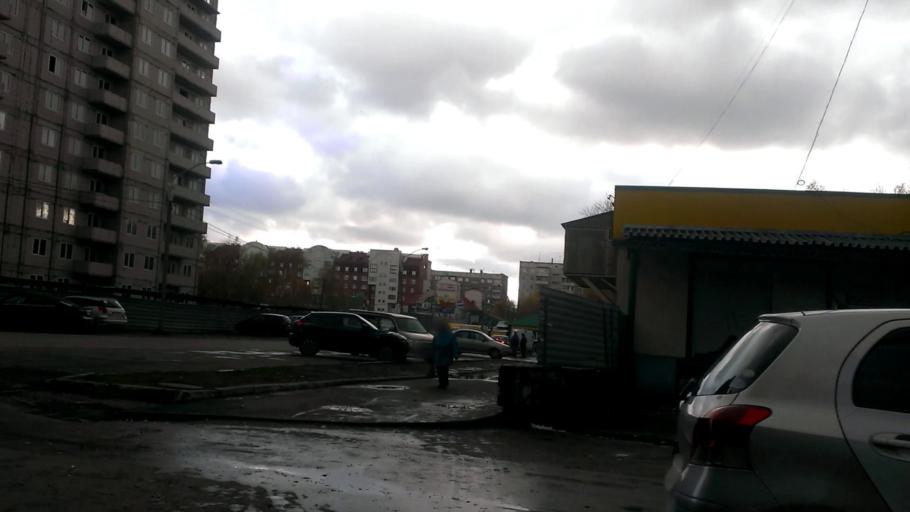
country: RU
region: Altai Krai
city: Novosilikatnyy
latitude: 53.3456
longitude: 83.6752
